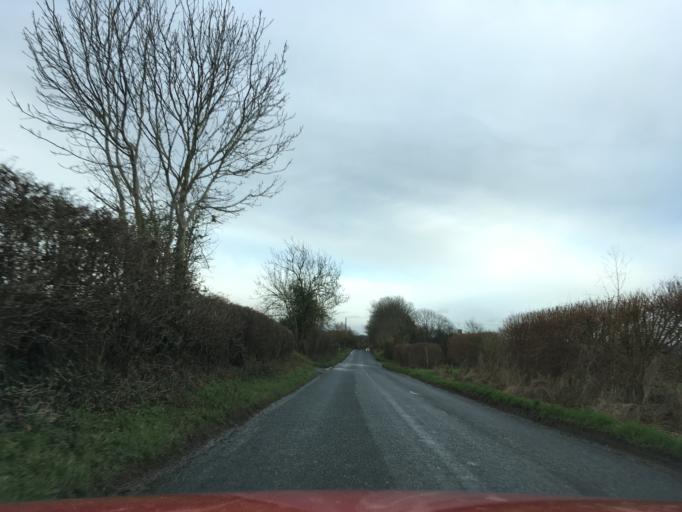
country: GB
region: England
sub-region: Worcestershire
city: Evesham
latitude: 52.0380
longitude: -1.9970
